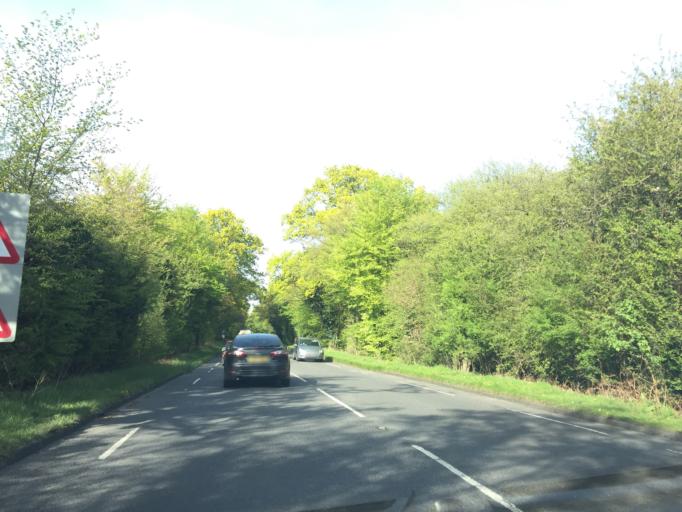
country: GB
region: England
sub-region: Essex
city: Theydon Bois
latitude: 51.6690
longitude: 0.0534
